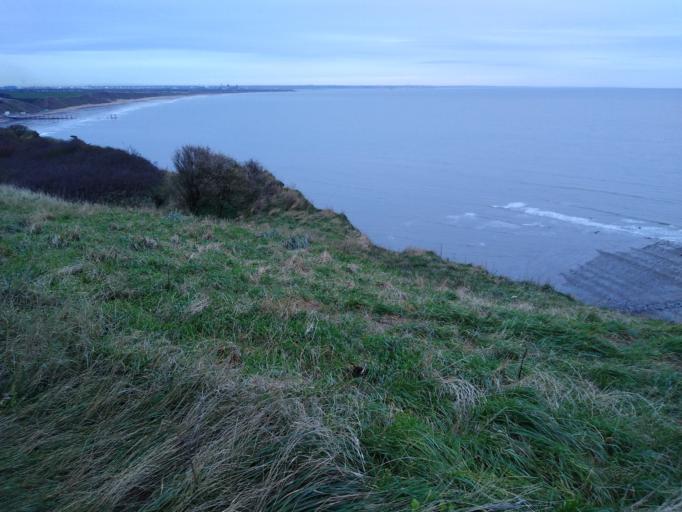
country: GB
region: England
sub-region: Redcar and Cleveland
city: Saltburn-by-the-Sea
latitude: 54.5863
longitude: -0.9493
